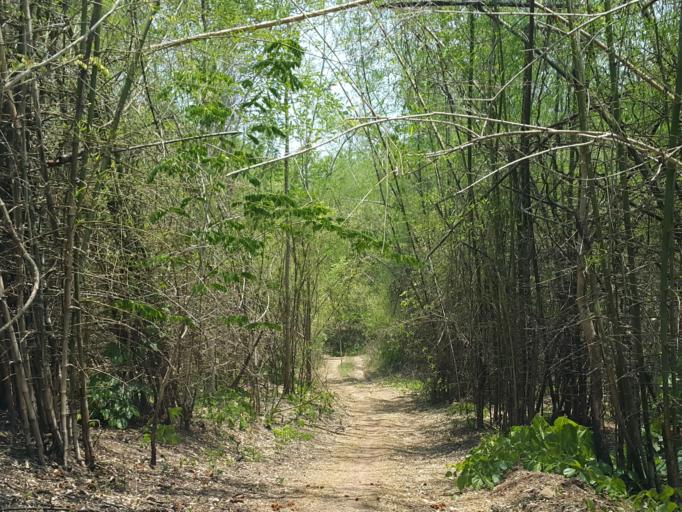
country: TH
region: Kanchanaburi
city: Sai Yok
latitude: 14.2189
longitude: 98.8780
